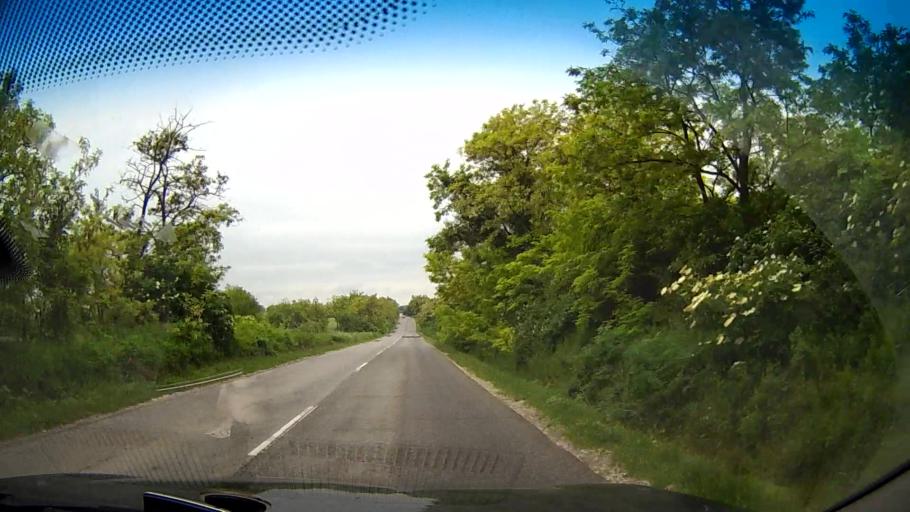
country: HU
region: Pest
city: Perbal
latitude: 47.5829
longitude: 18.7481
